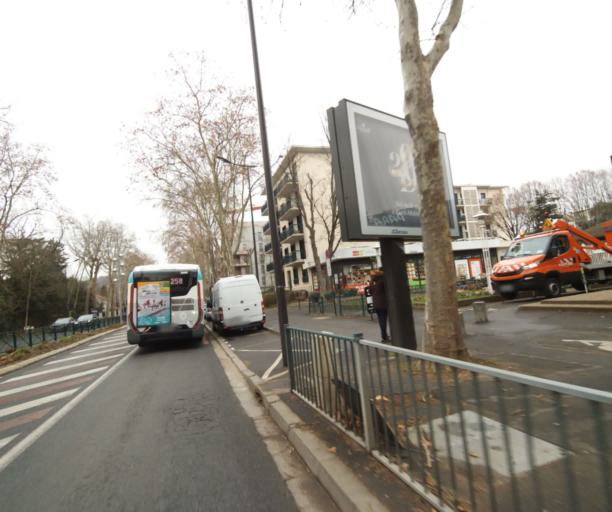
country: FR
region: Ile-de-France
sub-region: Departement des Yvelines
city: Chatou
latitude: 48.8732
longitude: 2.1642
